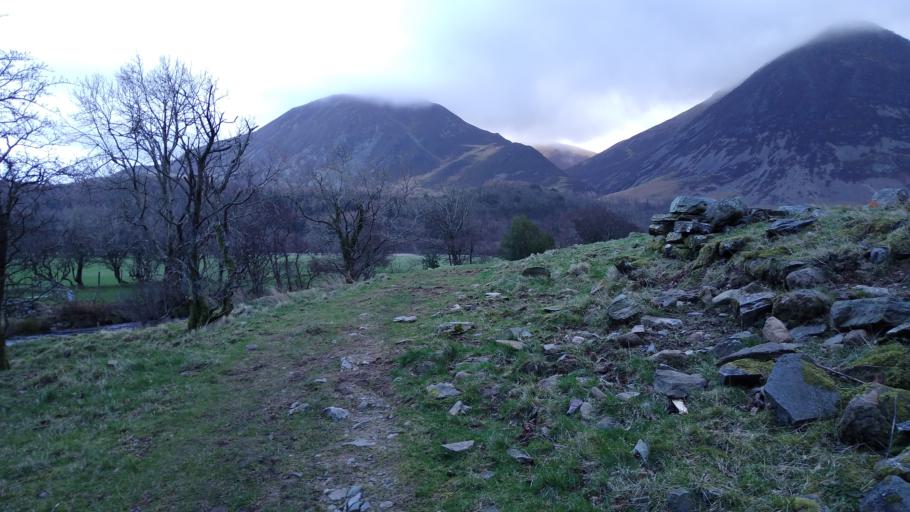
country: GB
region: England
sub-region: Cumbria
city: Cockermouth
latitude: 54.5727
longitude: -3.3225
